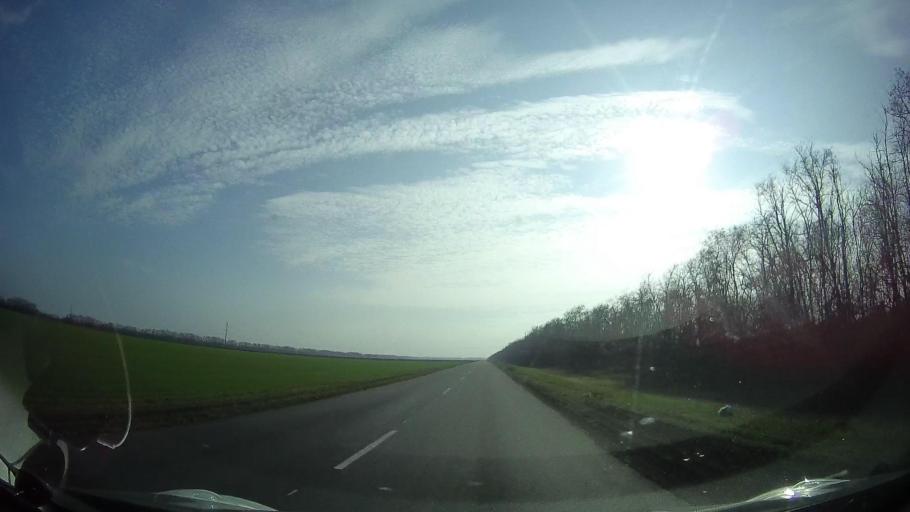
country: RU
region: Rostov
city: Mechetinskaya
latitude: 46.8972
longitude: 40.5419
